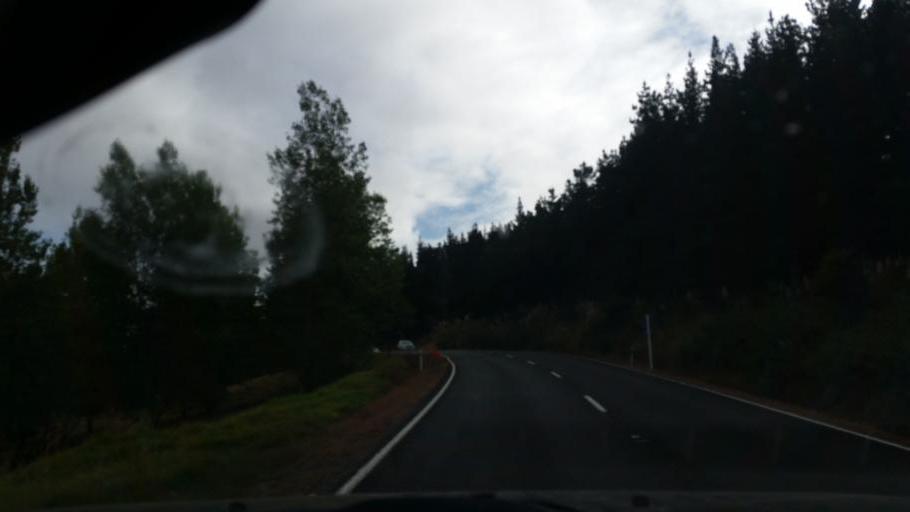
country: NZ
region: Auckland
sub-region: Auckland
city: Wellsford
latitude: -36.2074
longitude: 174.3927
